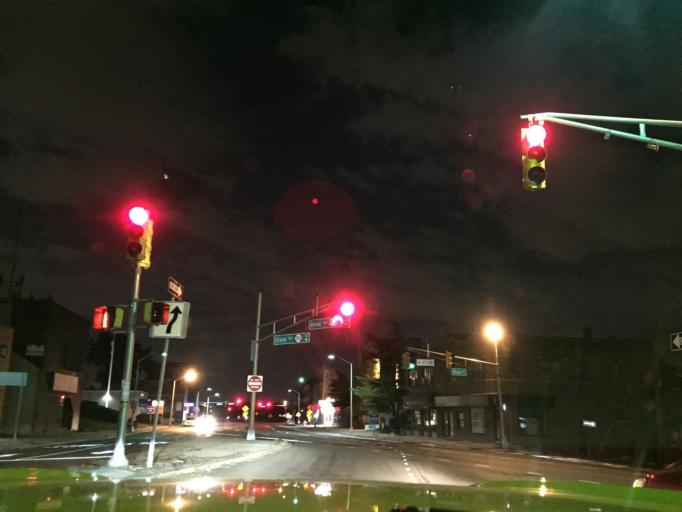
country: US
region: New Jersey
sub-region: Bergen County
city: Ridgefield
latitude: 40.8349
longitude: -74.0088
